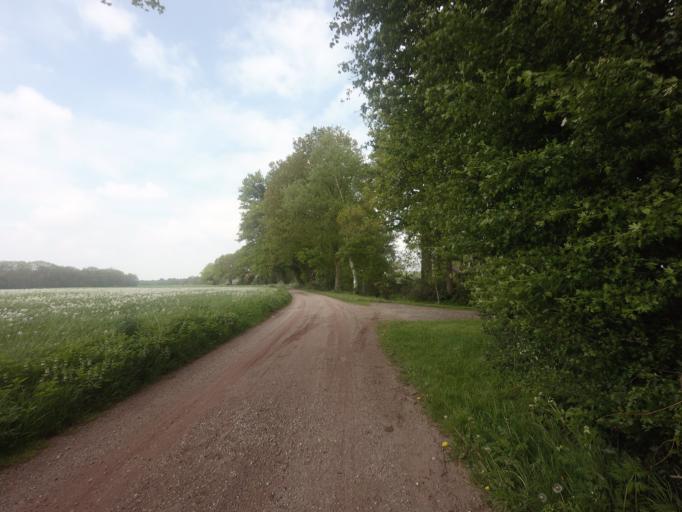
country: NL
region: Overijssel
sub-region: Gemeente Hof van Twente
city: Delden
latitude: 52.2124
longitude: 6.7312
